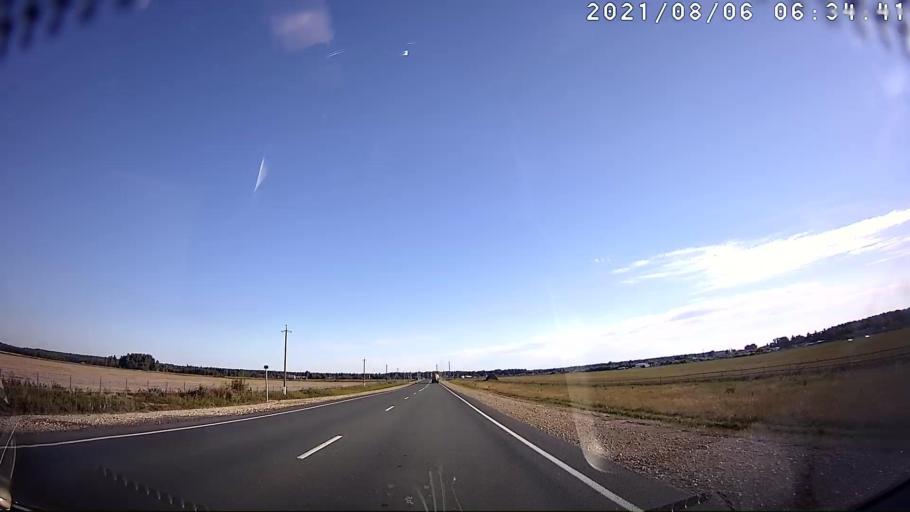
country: RU
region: Mariy-El
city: Krasnogorskiy
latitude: 56.2097
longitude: 48.2365
